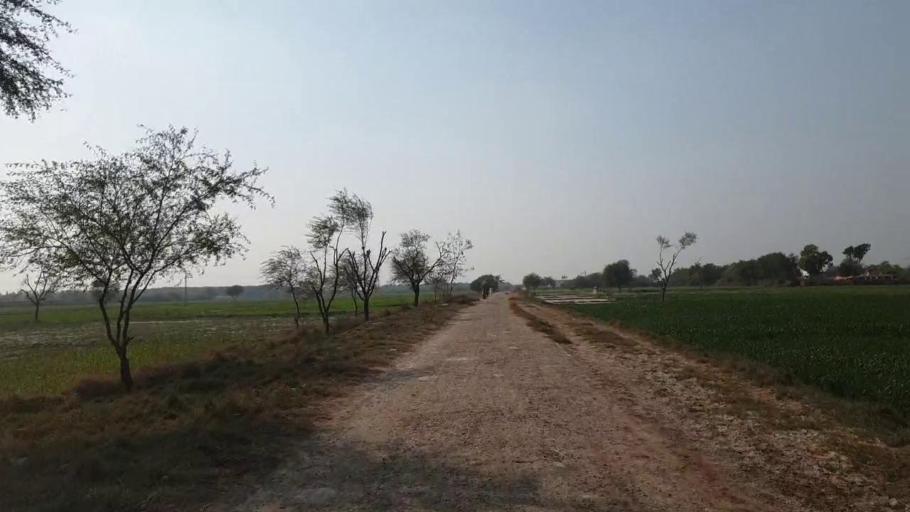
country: PK
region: Sindh
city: Tando Adam
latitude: 25.7157
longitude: 68.5679
